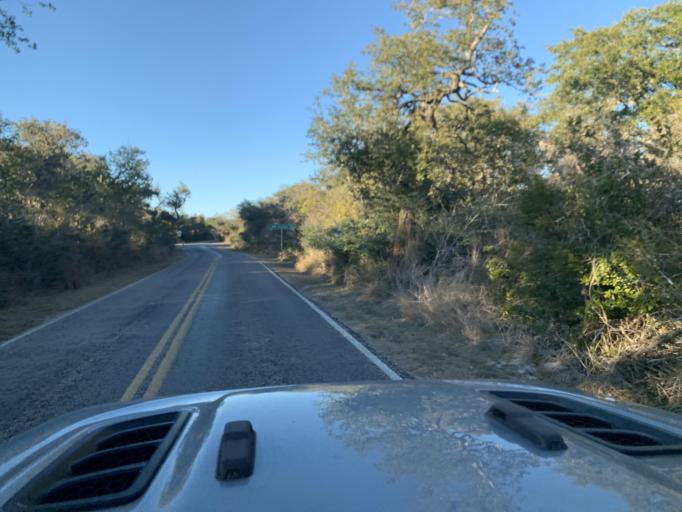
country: US
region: Texas
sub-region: Aransas County
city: Fulton
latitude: 28.1463
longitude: -96.9842
